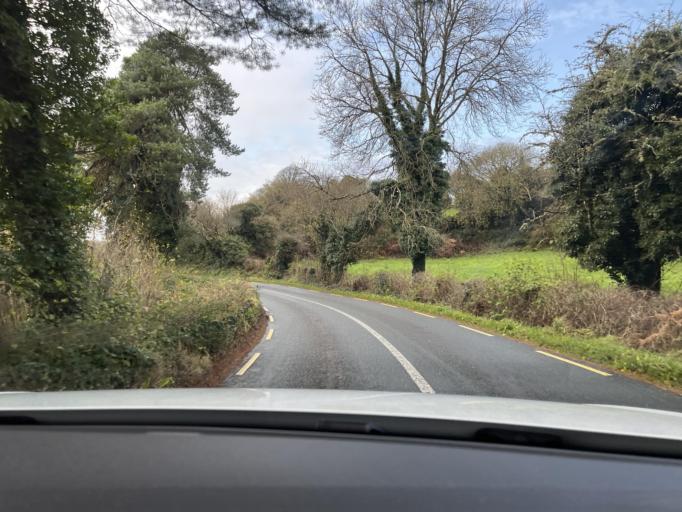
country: IE
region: Connaught
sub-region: Sligo
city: Sligo
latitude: 54.2658
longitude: -8.3371
